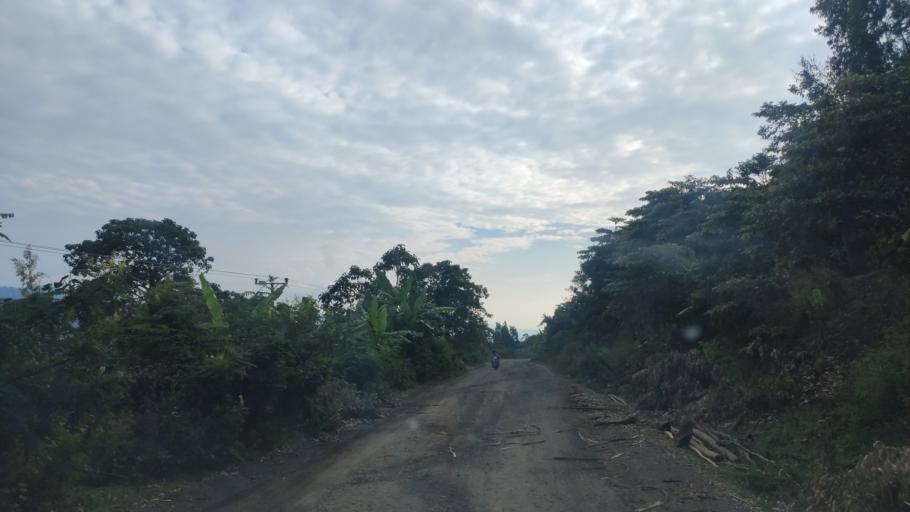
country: ET
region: Southern Nations, Nationalities, and People's Region
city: Arba Minch'
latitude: 6.4443
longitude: 37.3942
